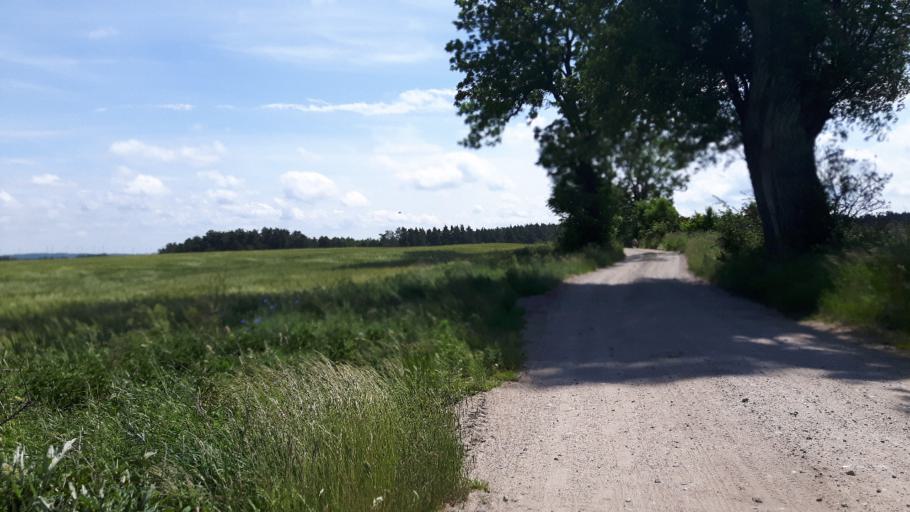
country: PL
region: Pomeranian Voivodeship
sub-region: Powiat wejherowski
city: Choczewo
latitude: 54.7463
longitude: 17.9468
